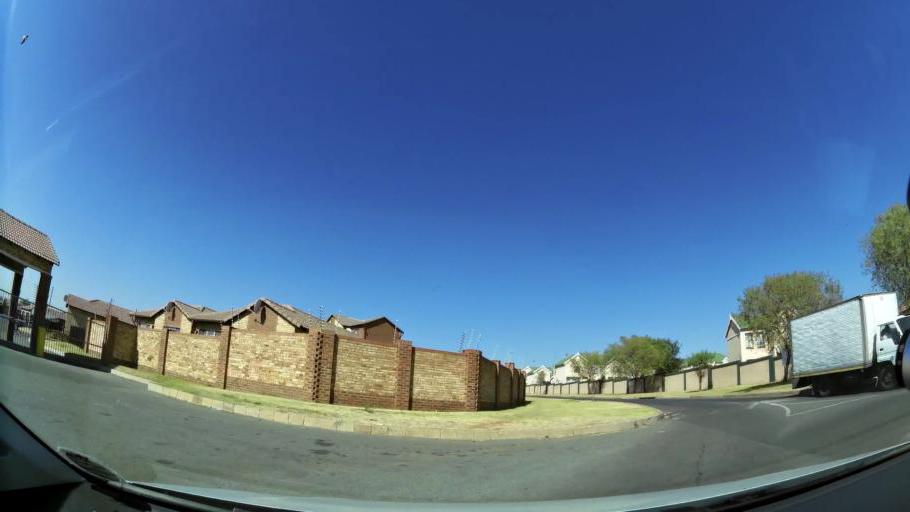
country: ZA
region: Gauteng
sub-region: City of Johannesburg Metropolitan Municipality
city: Modderfontein
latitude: -26.0736
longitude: 28.1945
